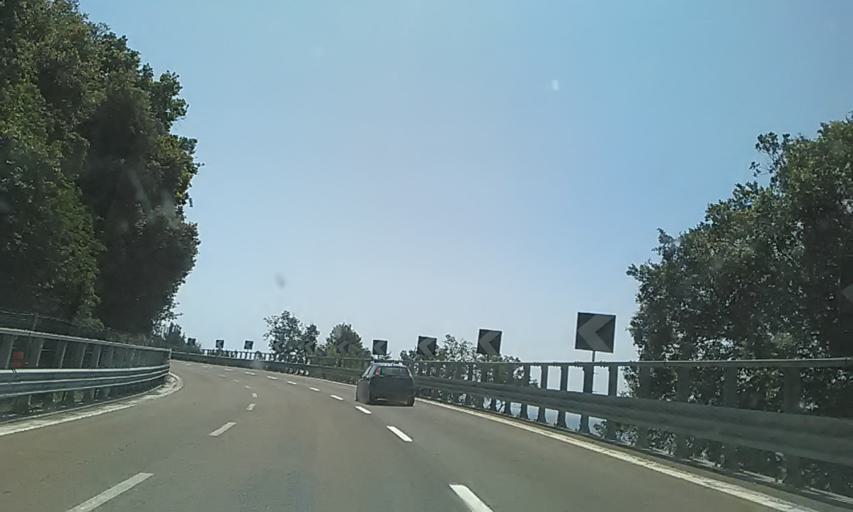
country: IT
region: Liguria
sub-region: Provincia di Genova
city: Arenzano
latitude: 44.4178
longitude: 8.7179
